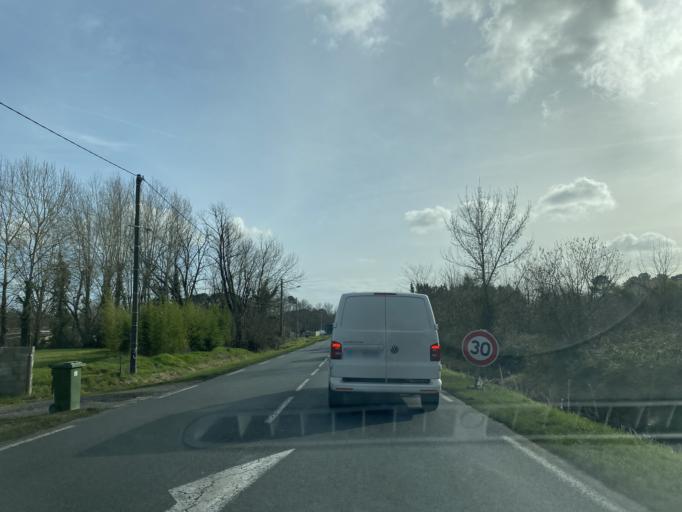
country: FR
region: Aquitaine
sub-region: Departement de la Gironde
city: Le Taillan-Medoc
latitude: 44.9234
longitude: -0.6753
